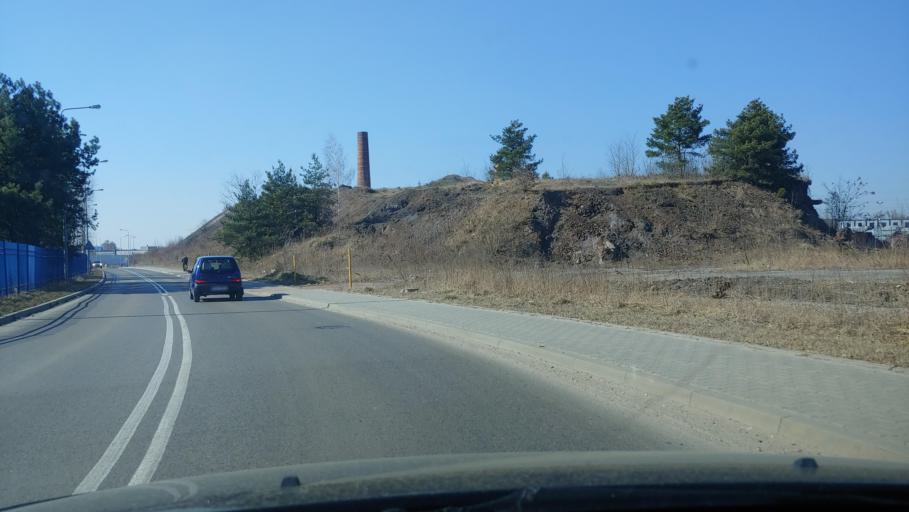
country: PL
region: Lesser Poland Voivodeship
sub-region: Powiat chrzanowski
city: Trzebinia
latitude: 50.1532
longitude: 19.4644
